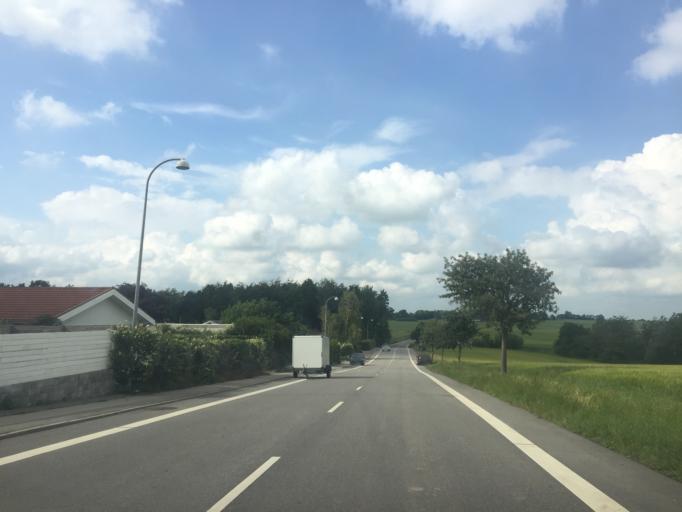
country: DK
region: Zealand
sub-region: Roskilde Kommune
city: Gundsomagle
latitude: 55.6962
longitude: 12.1601
